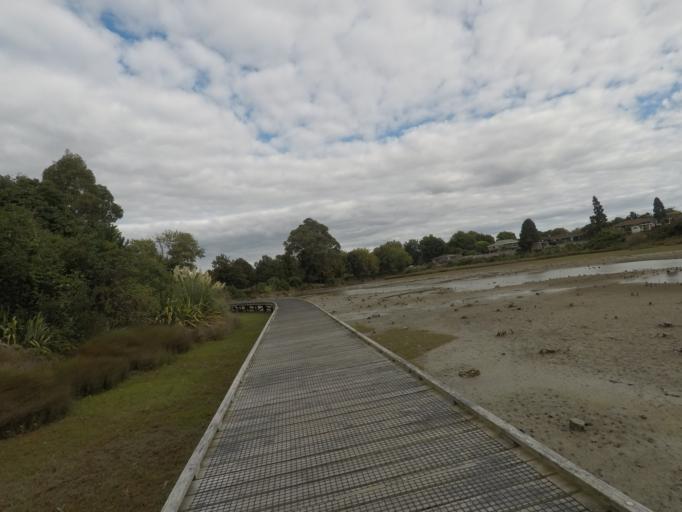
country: NZ
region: Auckland
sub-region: Auckland
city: Papakura
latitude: -37.0642
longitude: 174.9333
